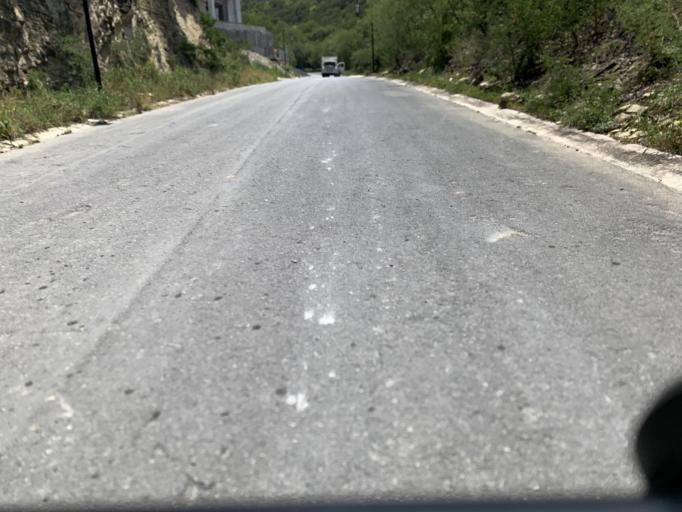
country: MX
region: Nuevo Leon
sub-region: Juarez
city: Bosques de San Pedro
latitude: 25.5124
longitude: -100.1814
